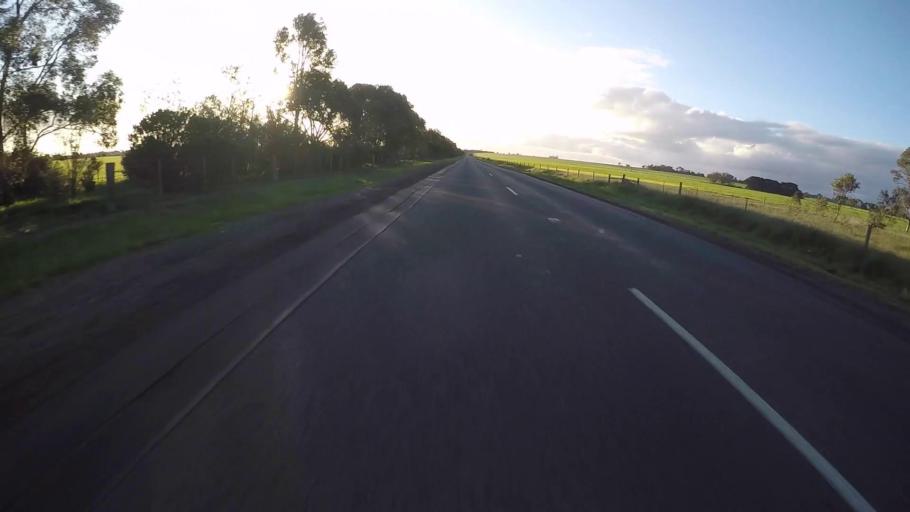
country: AU
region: Victoria
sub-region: Greater Geelong
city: Hamlyn Heights
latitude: -38.1282
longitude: 144.2803
